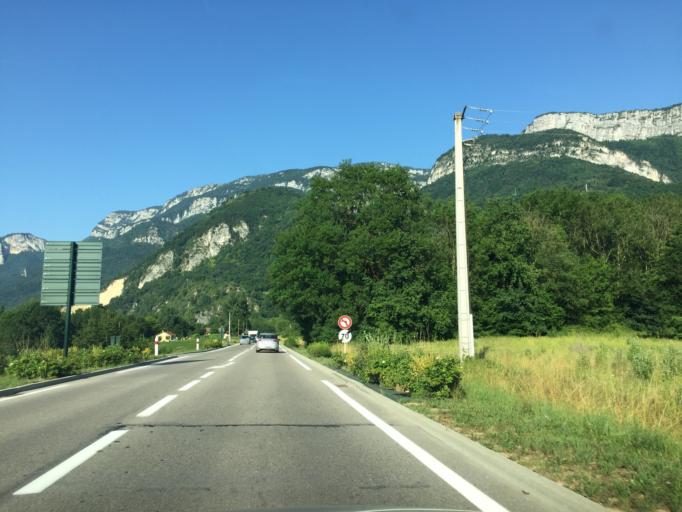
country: FR
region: Rhone-Alpes
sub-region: Departement de l'Isere
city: Vinay
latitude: 45.2049
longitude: 5.4740
